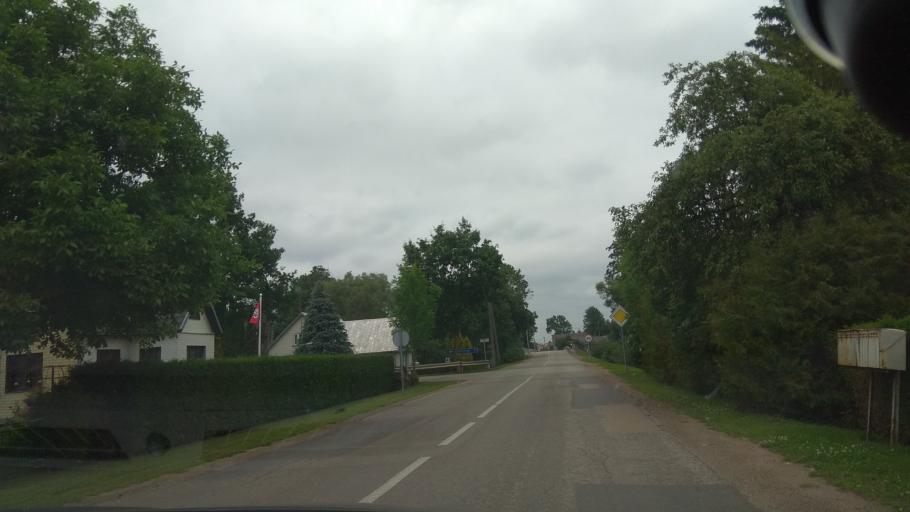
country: LT
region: Siauliu apskritis
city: Pakruojis
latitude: 55.9476
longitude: 23.9415
